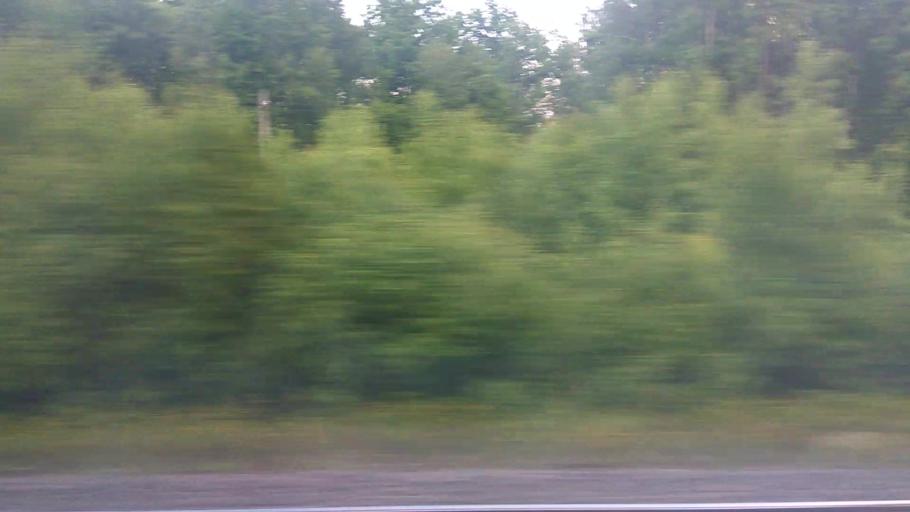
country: RU
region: Moskovskaya
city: Mikhnevo
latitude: 55.0785
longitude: 37.9770
